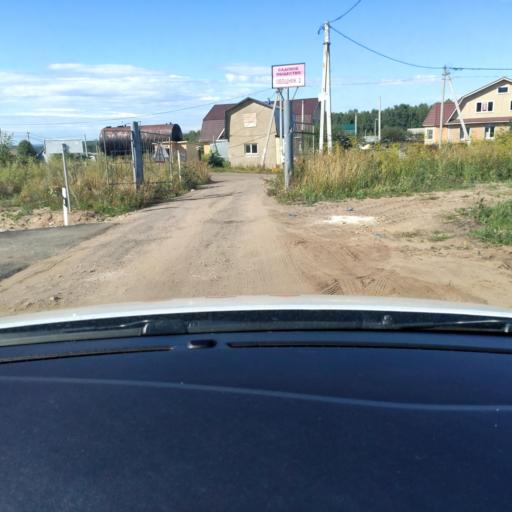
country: RU
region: Tatarstan
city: Vysokaya Gora
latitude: 55.8029
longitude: 49.2930
